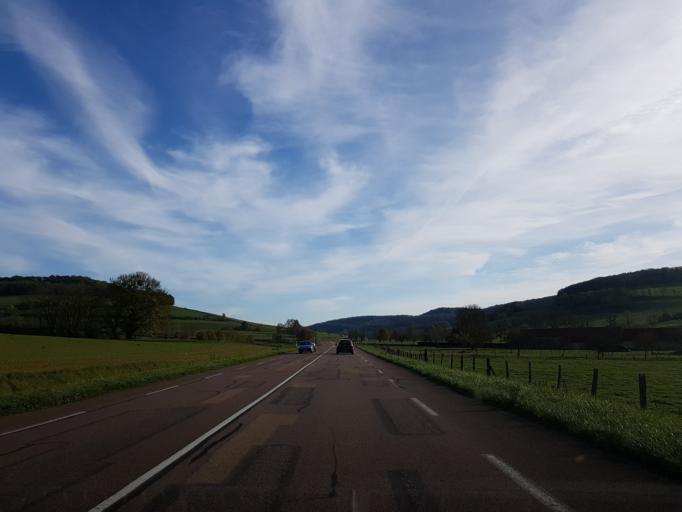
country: FR
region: Bourgogne
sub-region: Departement de la Cote-d'Or
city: Vitteaux
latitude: 47.3466
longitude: 4.5773
